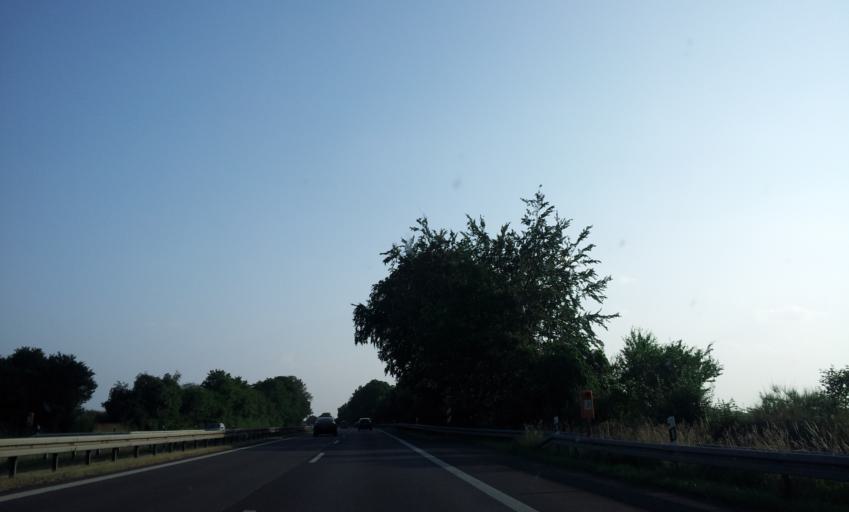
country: DE
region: Brandenburg
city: Marienwerder
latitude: 52.8666
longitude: 13.6821
